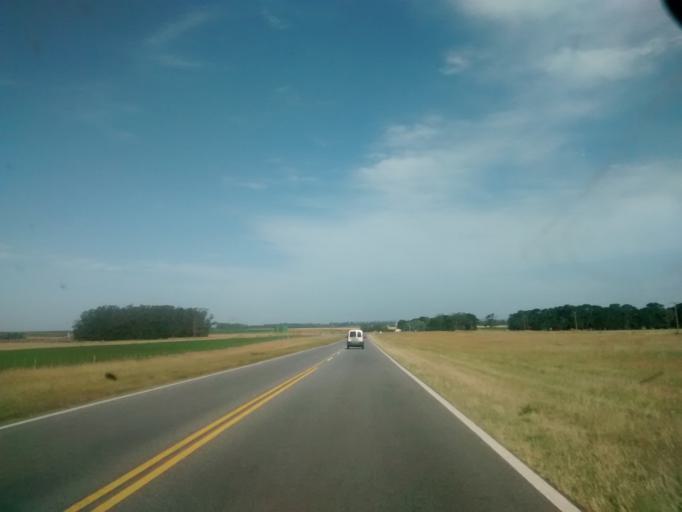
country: AR
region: Buenos Aires
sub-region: Partido de Balcarce
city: Balcarce
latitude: -37.6479
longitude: -58.5777
